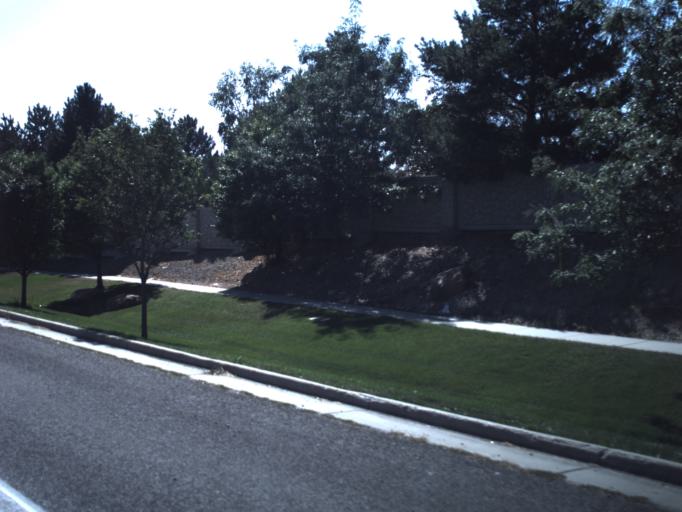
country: US
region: Utah
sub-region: Cache County
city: Smithfield
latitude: 41.8508
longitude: -111.8321
